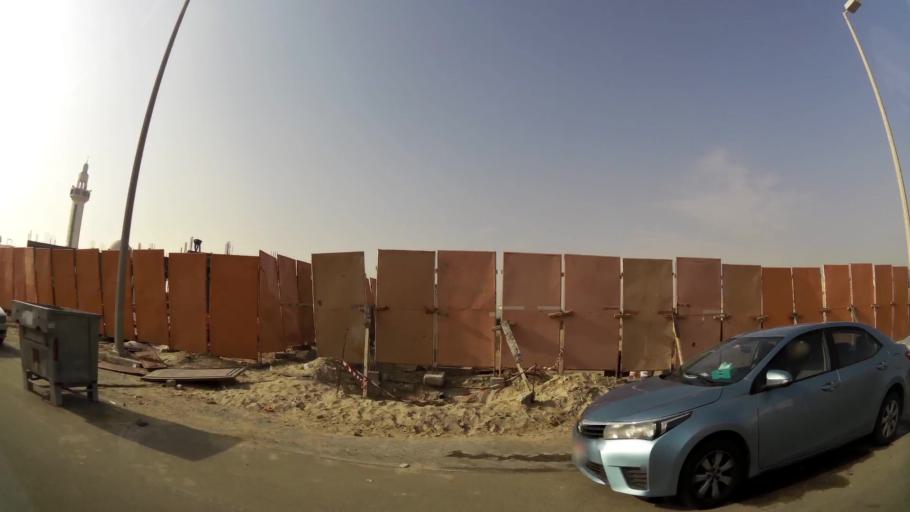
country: AE
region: Abu Dhabi
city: Abu Dhabi
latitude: 24.2701
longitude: 54.6592
